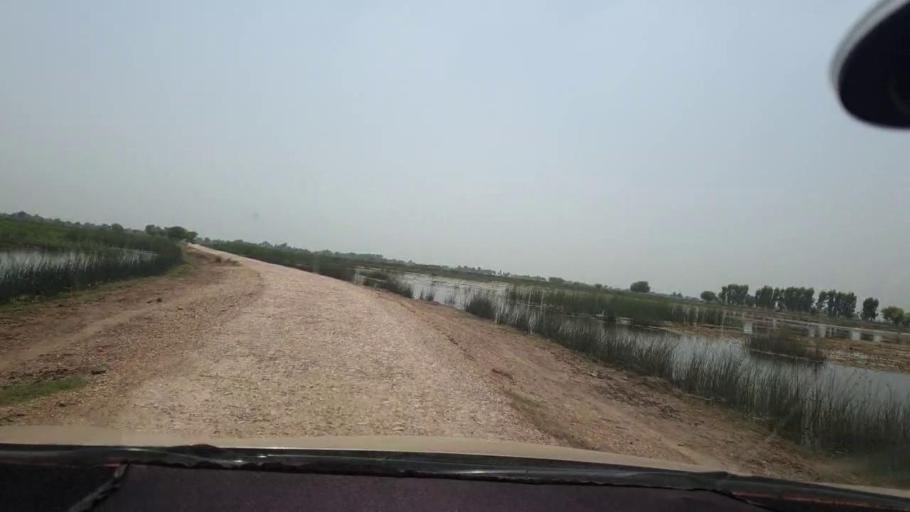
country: PK
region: Sindh
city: Kambar
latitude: 27.6490
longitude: 67.9322
